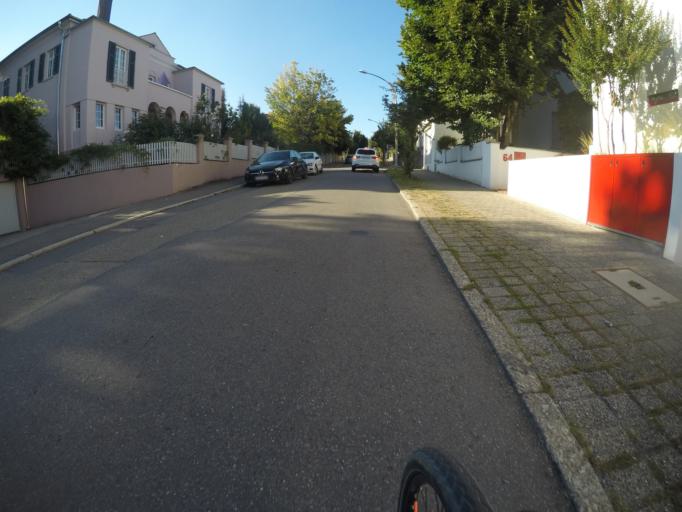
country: DE
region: Baden-Wuerttemberg
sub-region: Regierungsbezirk Stuttgart
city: Stuttgart Feuerbach
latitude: 48.8131
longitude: 9.1545
